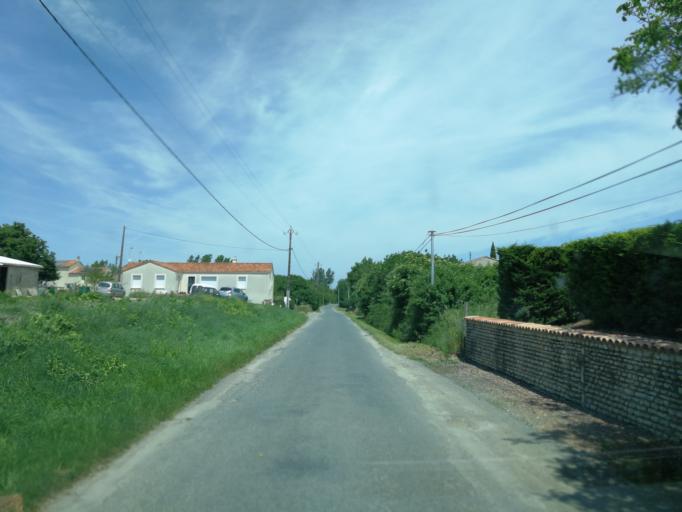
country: FR
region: Pays de la Loire
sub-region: Departement de la Vendee
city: Le Langon
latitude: 46.3849
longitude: -0.9407
